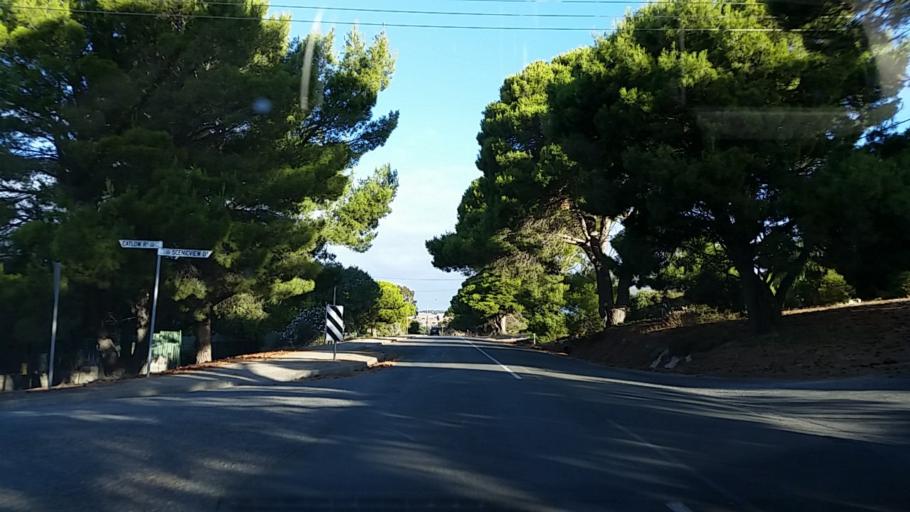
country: AU
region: South Australia
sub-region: Yankalilla
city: Normanville
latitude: -35.5152
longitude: 138.2192
